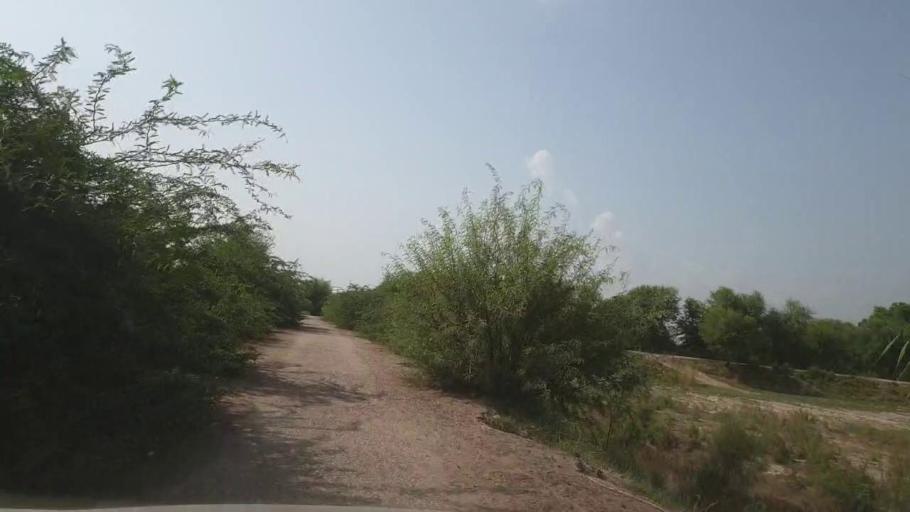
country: PK
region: Sindh
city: Pano Aqil
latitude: 27.7700
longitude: 69.1666
